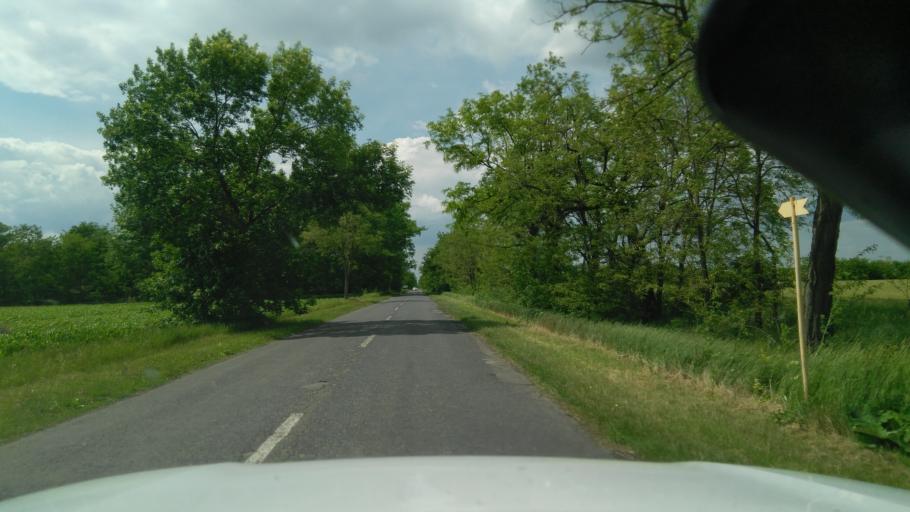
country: HU
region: Bekes
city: Magyarbanhegyes
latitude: 46.4681
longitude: 20.9462
